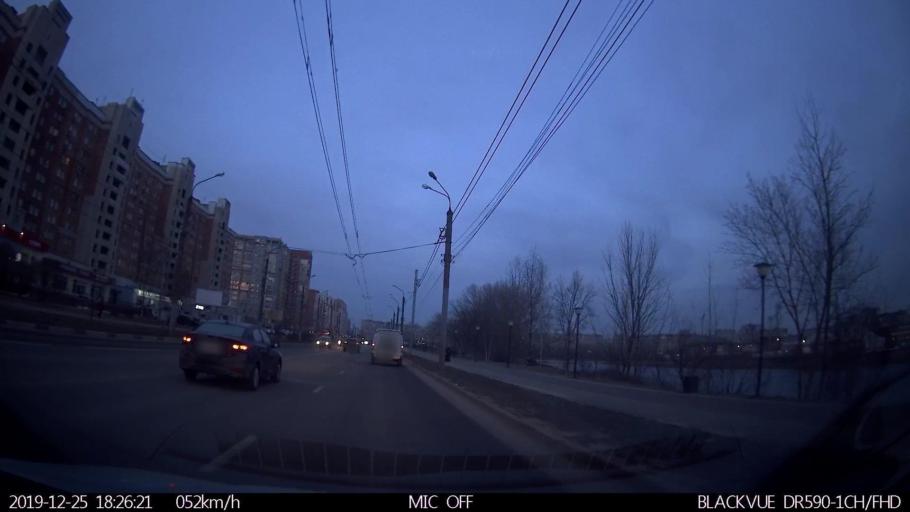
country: RU
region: Nizjnij Novgorod
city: Nizhniy Novgorod
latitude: 56.3364
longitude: 43.9406
